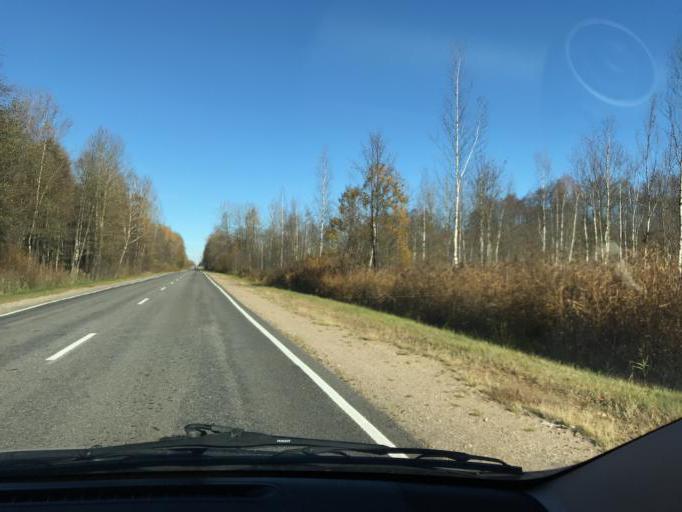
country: BY
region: Vitebsk
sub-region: Ushatski Rayon
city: Ushachy
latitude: 55.0746
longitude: 28.7545
